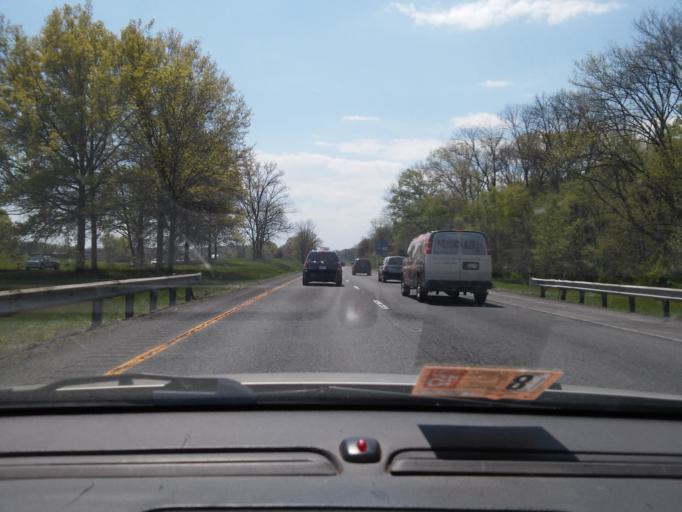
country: US
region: Maryland
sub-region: Washington County
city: Halfway
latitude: 39.6447
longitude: -77.7587
